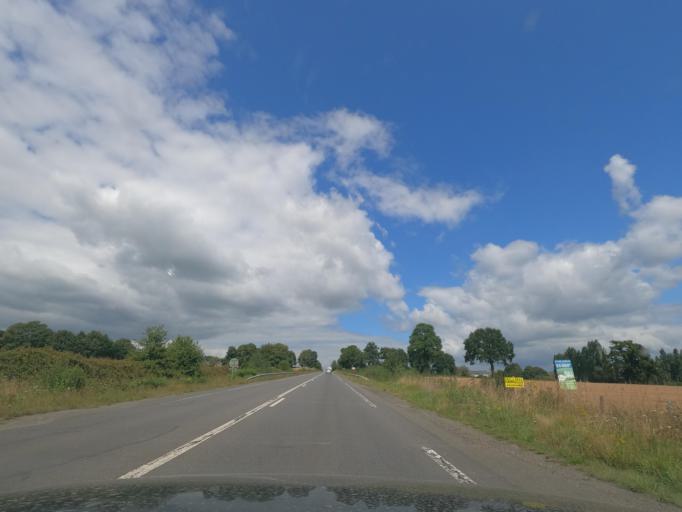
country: FR
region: Brittany
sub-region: Departement d'Ille-et-Vilaine
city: Lecousse
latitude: 48.3564
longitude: -1.2299
